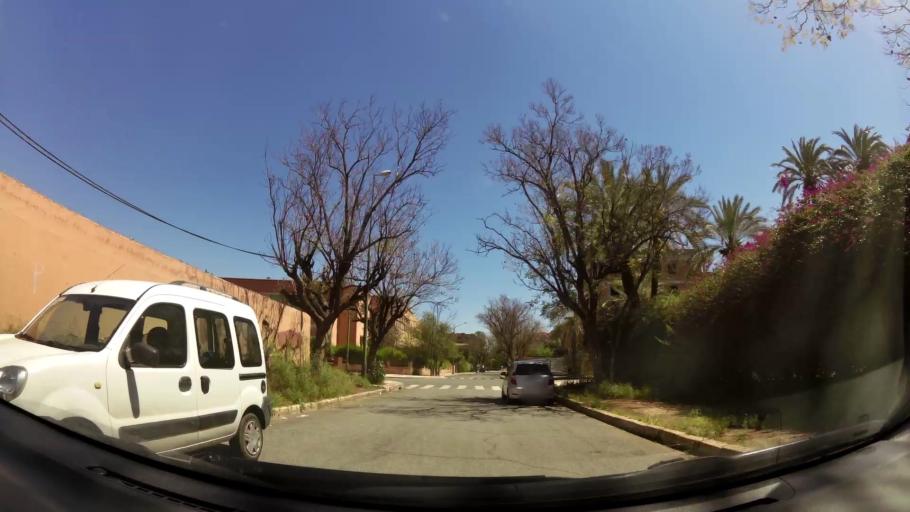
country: MA
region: Marrakech-Tensift-Al Haouz
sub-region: Marrakech
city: Marrakesh
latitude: 31.6261
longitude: -8.0065
